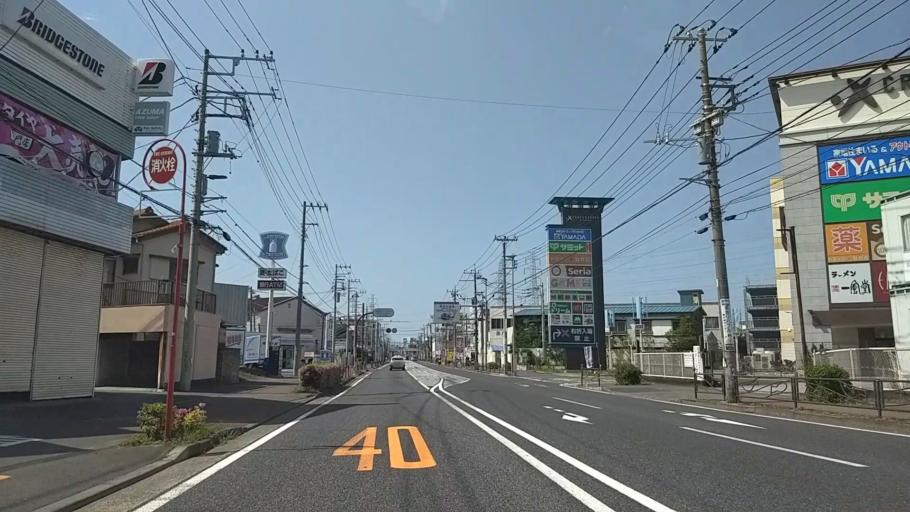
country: JP
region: Kanagawa
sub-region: Kawasaki-shi
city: Kawasaki
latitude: 35.5350
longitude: 139.6668
